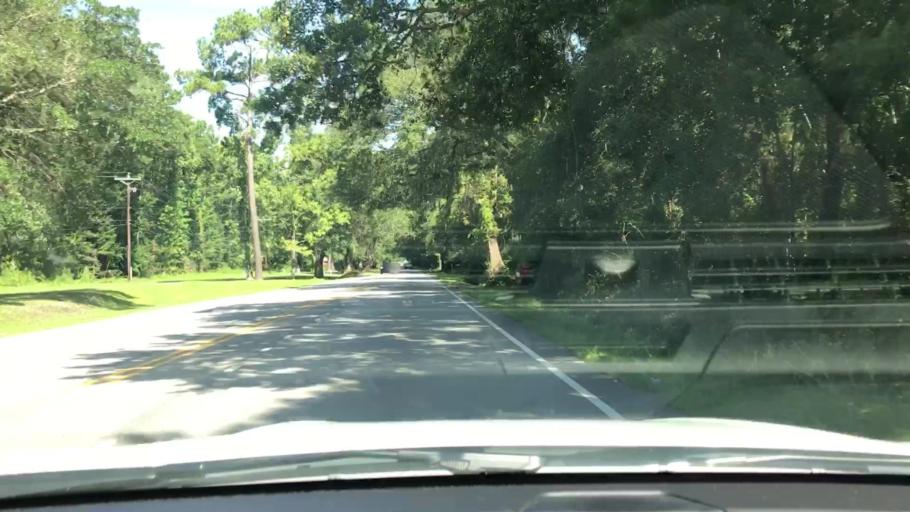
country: US
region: South Carolina
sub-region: Charleston County
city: Shell Point
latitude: 32.8468
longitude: -80.0621
